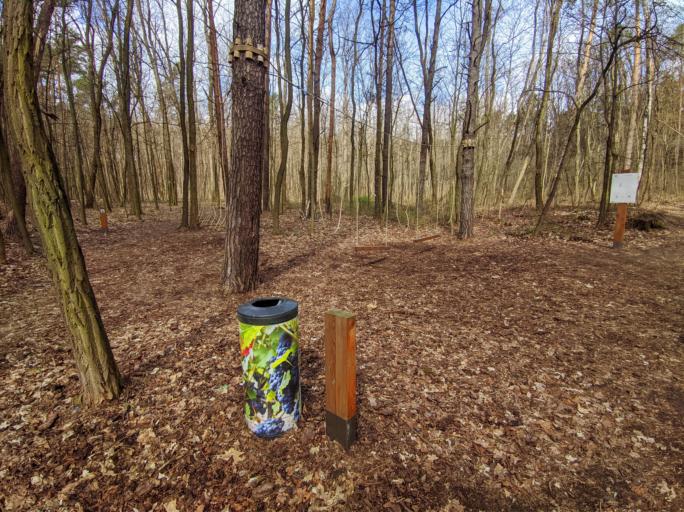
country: PL
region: Lubusz
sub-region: Zielona Gora
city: Zielona Gora
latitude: 51.9301
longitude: 15.5321
